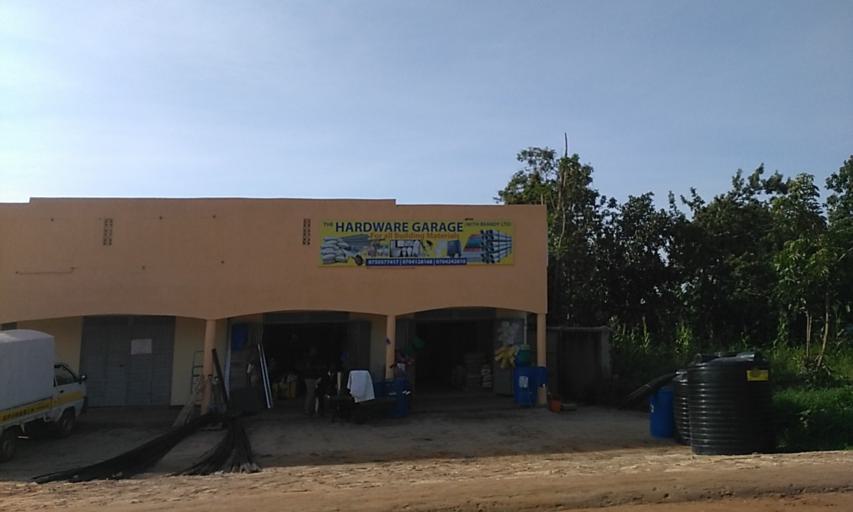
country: UG
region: Central Region
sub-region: Wakiso District
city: Bweyogerere
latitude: 0.4601
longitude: 32.6333
